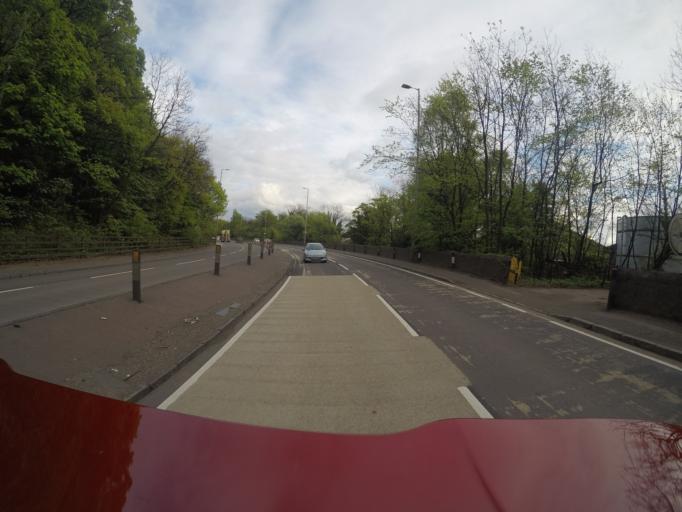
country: GB
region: Scotland
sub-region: West Dunbartonshire
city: Dumbarton
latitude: 55.9378
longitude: -4.5350
